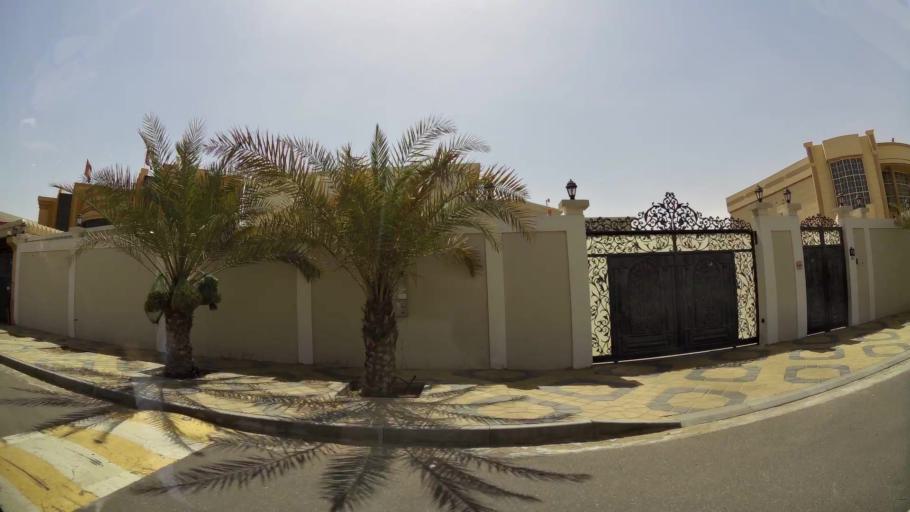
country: AE
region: Ash Shariqah
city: Sharjah
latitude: 25.1874
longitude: 55.4269
